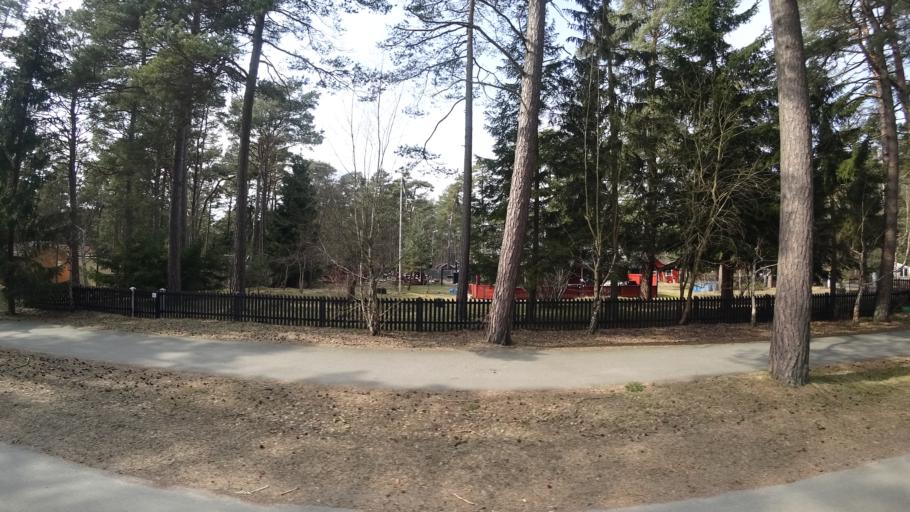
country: SE
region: Skane
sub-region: Kristianstads Kommun
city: Ahus
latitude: 55.9440
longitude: 14.3206
